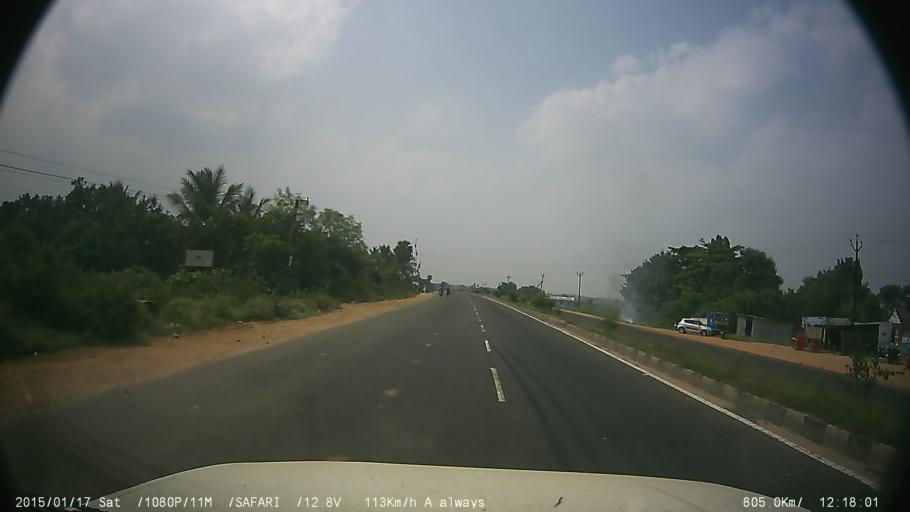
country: IN
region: Tamil Nadu
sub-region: Kancheepuram
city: Wallajahbad
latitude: 12.9085
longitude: 79.8356
